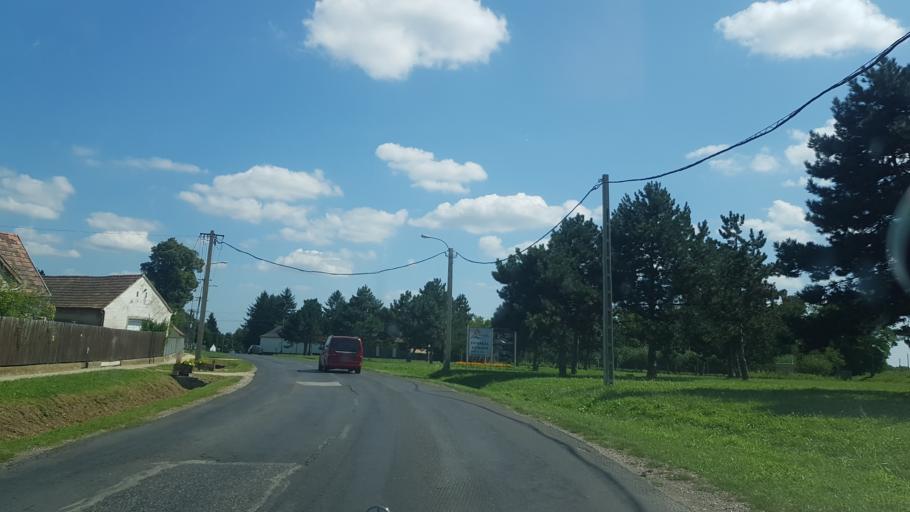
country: HU
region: Somogy
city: Marcali
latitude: 46.5437
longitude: 17.4133
